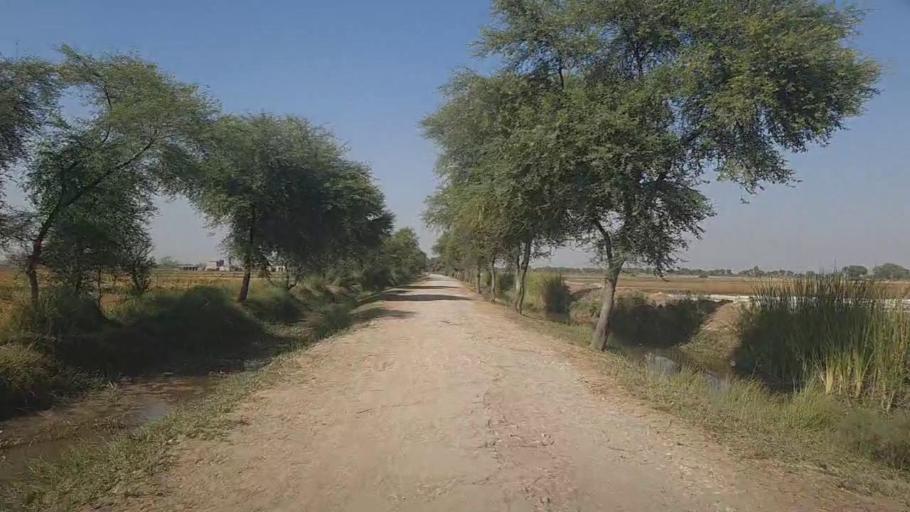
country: PK
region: Sindh
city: Thul
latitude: 28.3073
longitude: 68.7700
